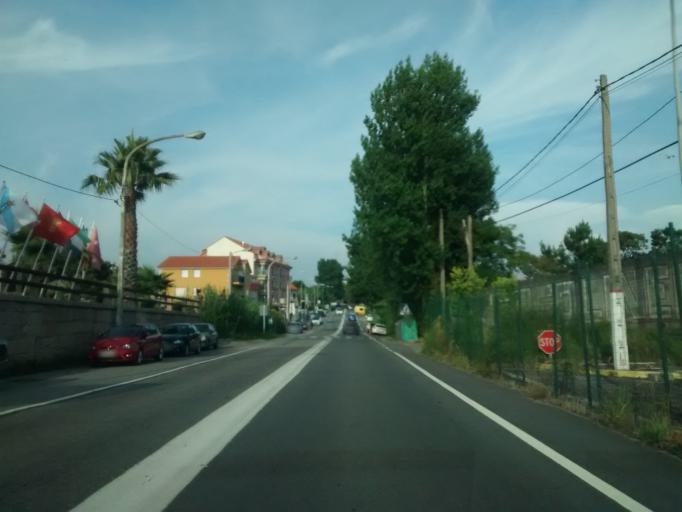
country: ES
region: Galicia
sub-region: Provincia de Pontevedra
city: Sanxenxo
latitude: 42.3920
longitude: -8.8339
